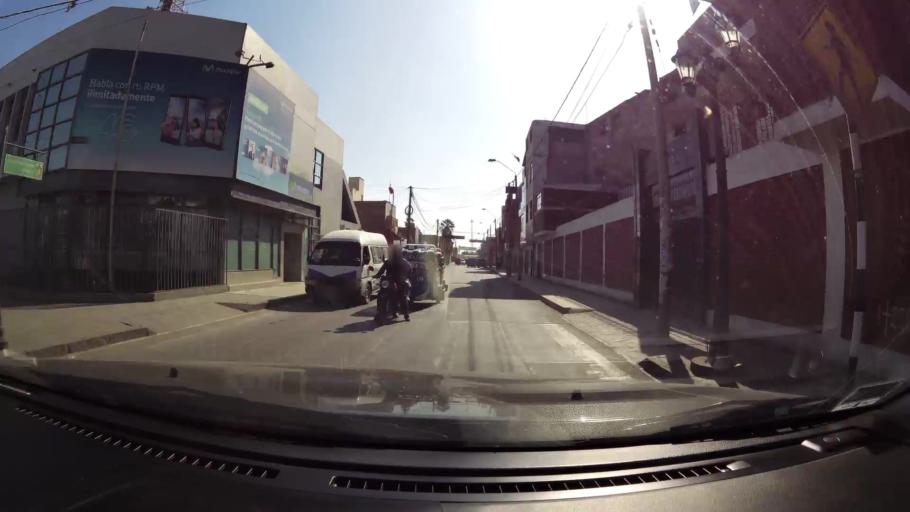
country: PE
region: Ica
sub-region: Provincia de Chincha
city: Chincha Alta
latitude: -13.4149
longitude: -76.1327
